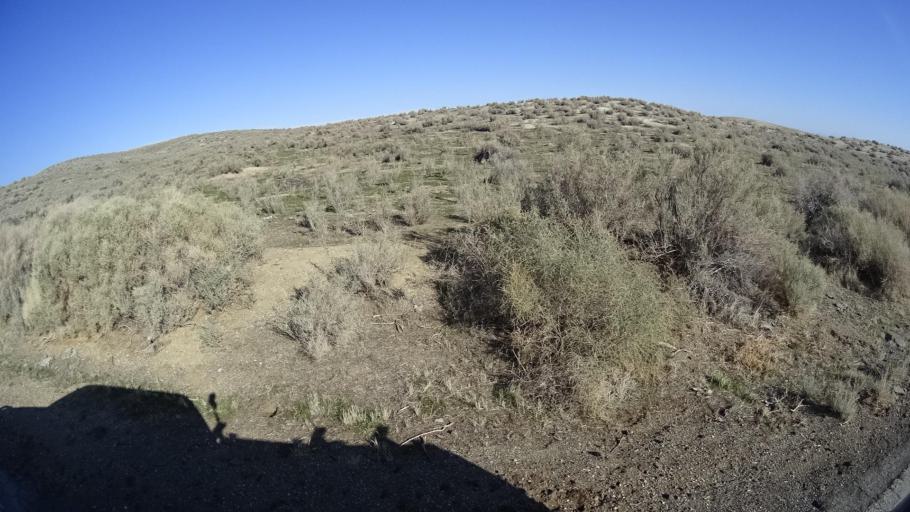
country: US
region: California
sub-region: Kern County
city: Taft Heights
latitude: 35.2315
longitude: -119.6498
